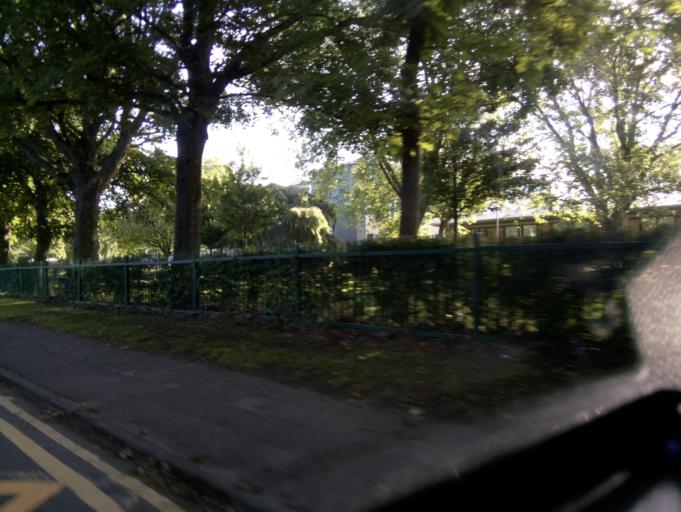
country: GB
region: England
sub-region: South Gloucestershire
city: Mangotsfield
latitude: 51.4791
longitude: -2.4845
